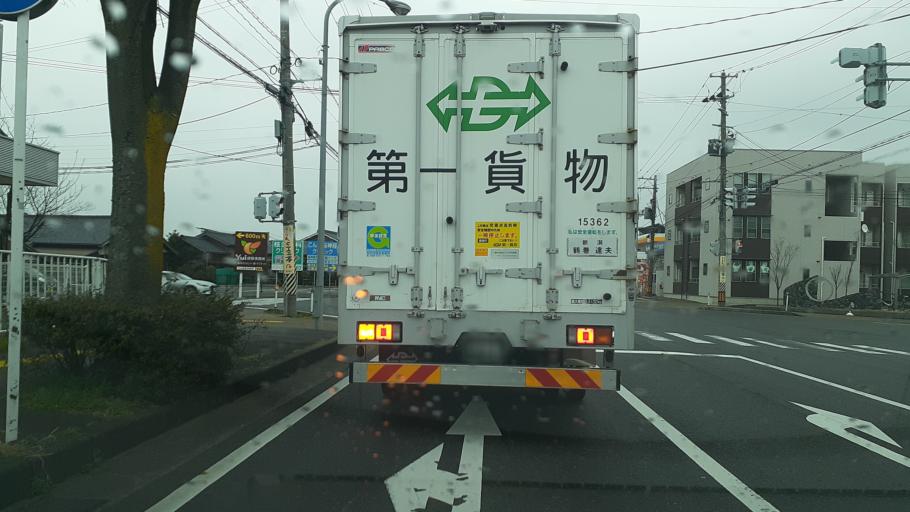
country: JP
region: Niigata
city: Kameda-honcho
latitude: 37.8716
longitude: 139.0936
